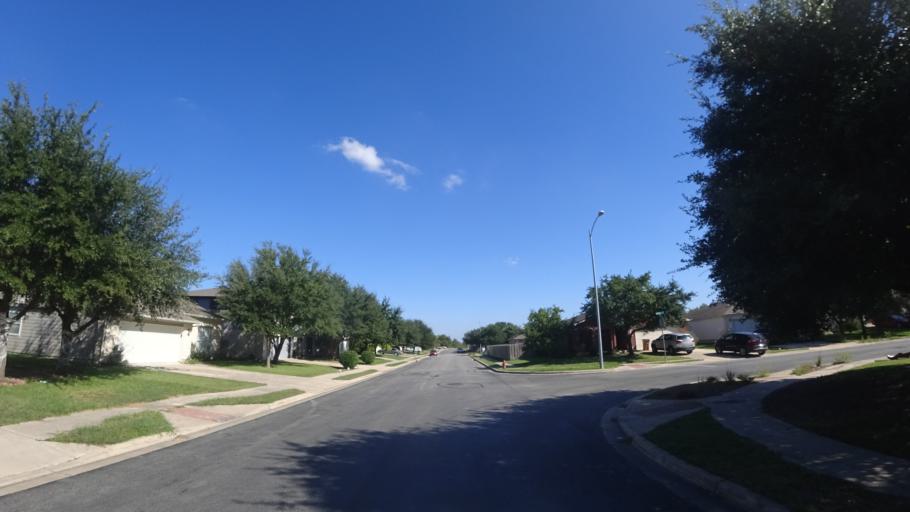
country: US
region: Texas
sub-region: Travis County
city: Manor
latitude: 30.3657
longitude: -97.6104
